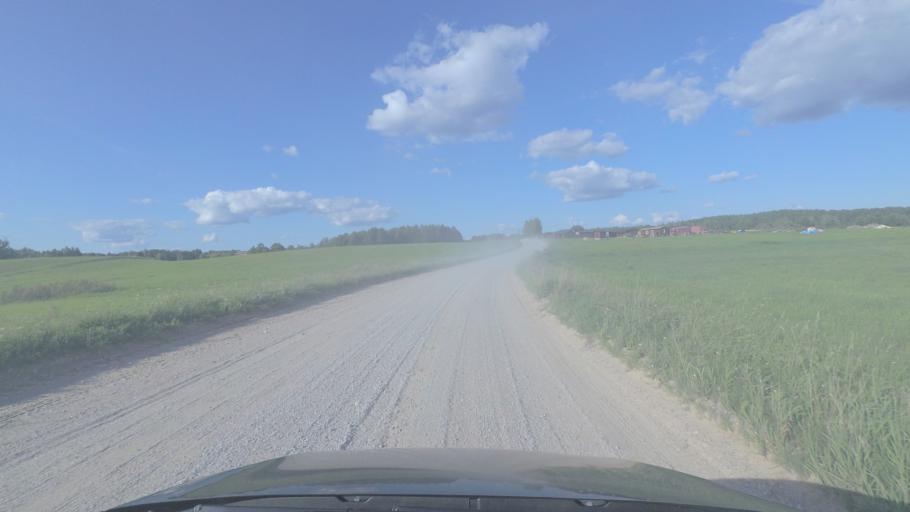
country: LT
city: Pabrade
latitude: 55.1352
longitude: 25.7081
